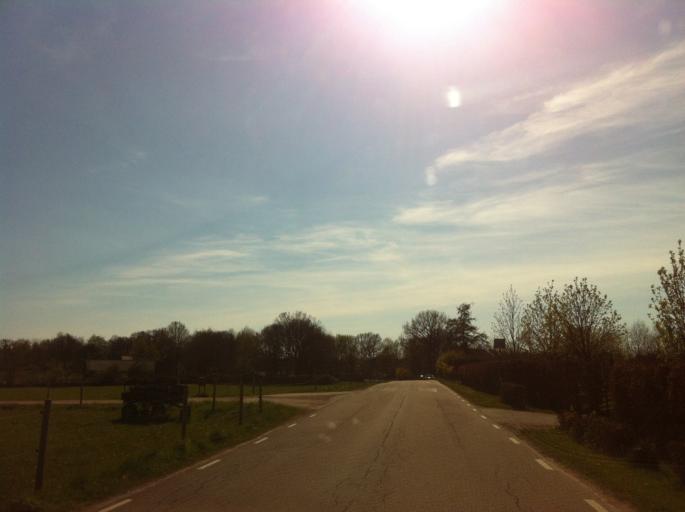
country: SE
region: Skane
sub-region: Svalovs Kommun
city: Kagerod
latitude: 56.0664
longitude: 13.1163
